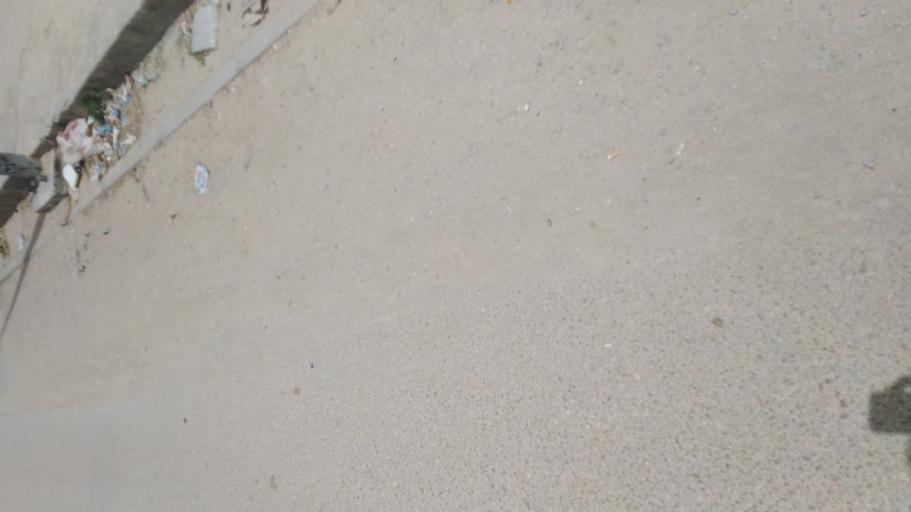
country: TN
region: Al Qayrawan
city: Kairouan
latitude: 35.6642
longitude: 10.0984
